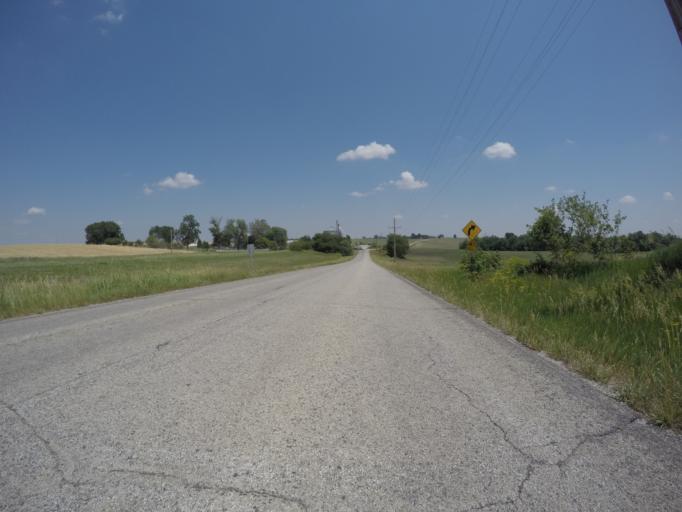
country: US
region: Kansas
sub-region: Doniphan County
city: Troy
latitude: 39.7682
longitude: -95.1201
